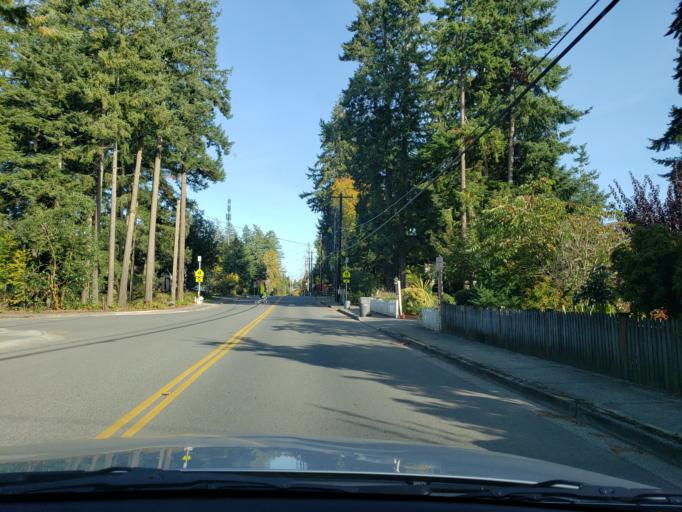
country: US
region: Washington
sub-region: Snohomish County
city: Meadowdale
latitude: 47.8717
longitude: -122.3127
